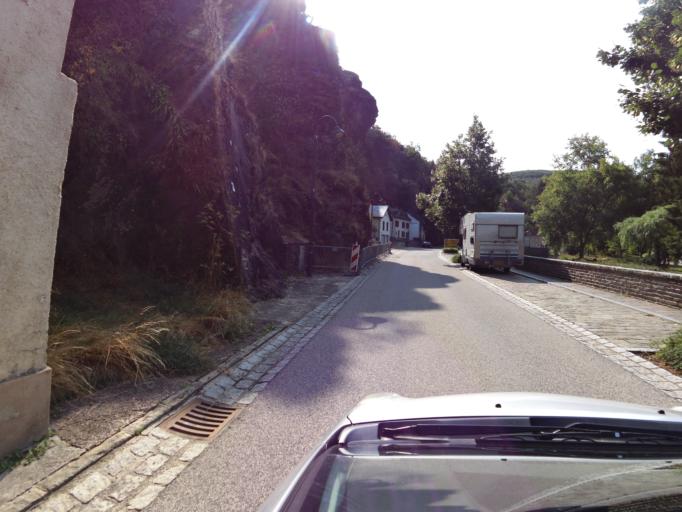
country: LU
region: Diekirch
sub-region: Canton de Wiltz
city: Esch-sur-Sure
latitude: 49.9110
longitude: 5.9337
